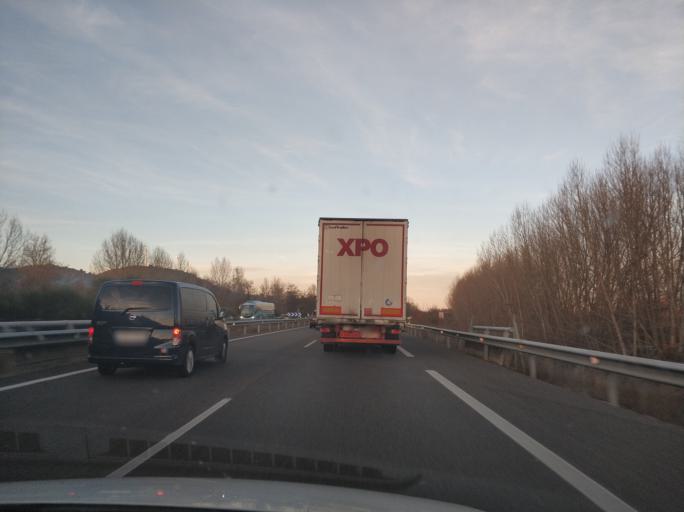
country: ES
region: Castille and Leon
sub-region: Provincia de Palencia
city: Duenas
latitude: 41.8787
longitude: -4.5402
